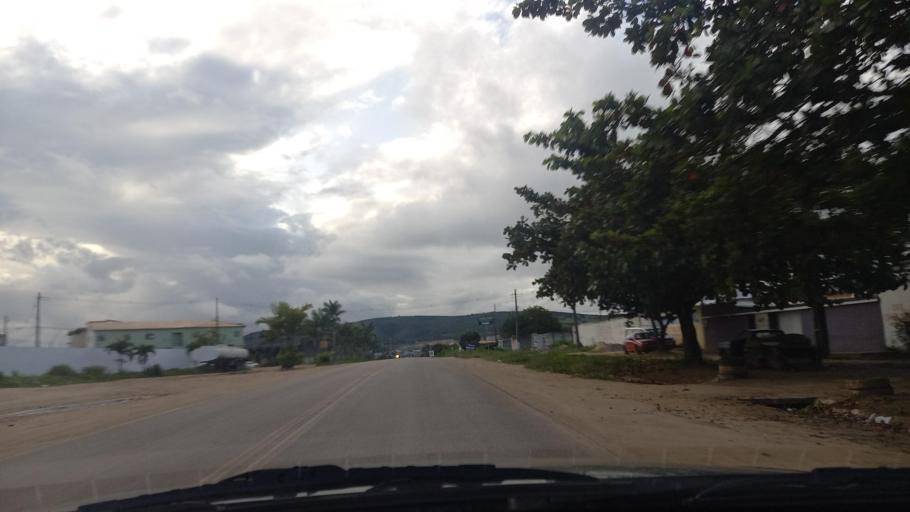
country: BR
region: Pernambuco
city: Garanhuns
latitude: -8.9045
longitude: -36.4995
